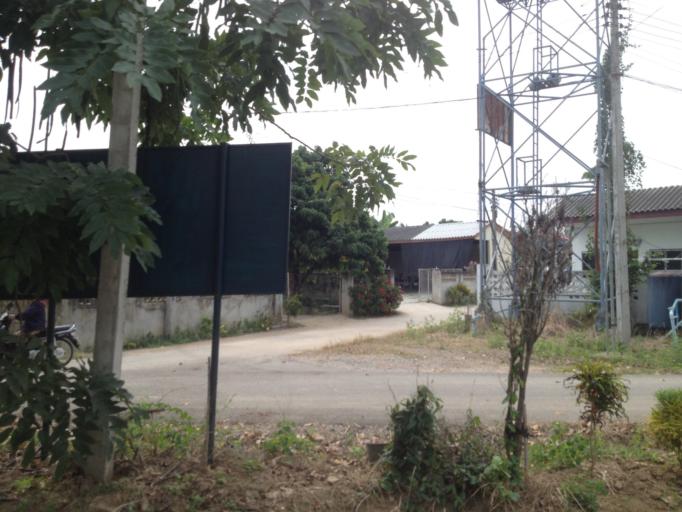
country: TH
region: Chiang Mai
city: Hang Dong
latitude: 18.6878
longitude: 98.9011
